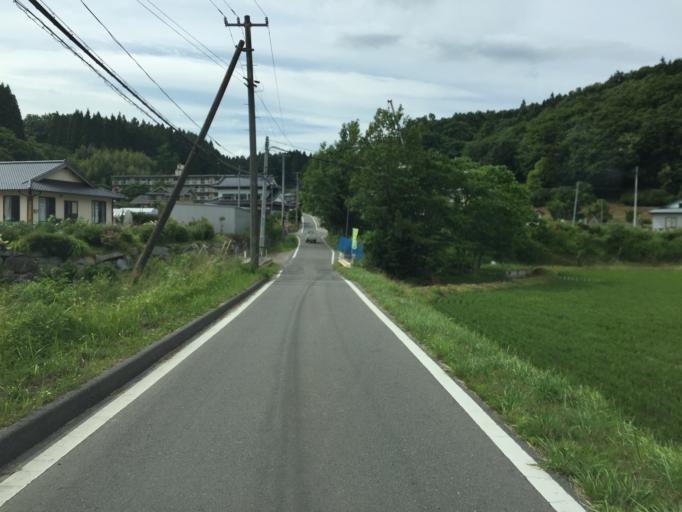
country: JP
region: Fukushima
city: Funehikimachi-funehiki
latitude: 37.4417
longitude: 140.6411
